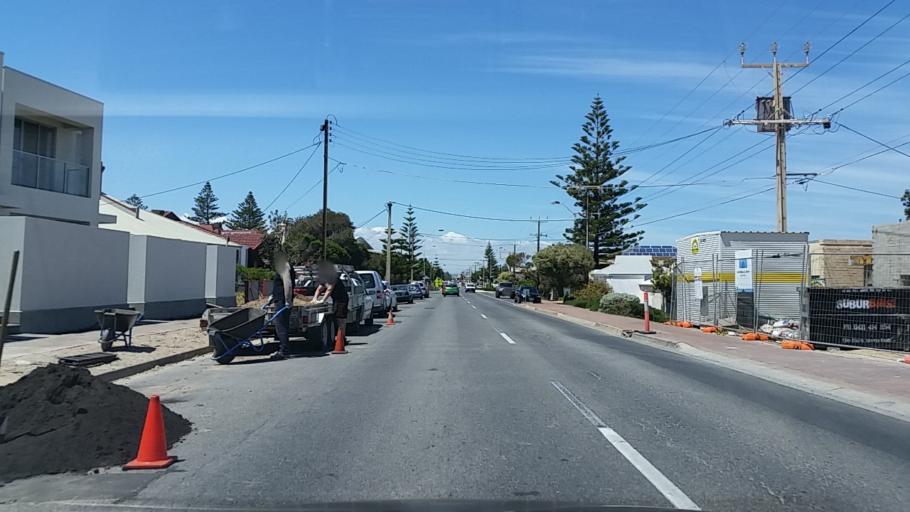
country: AU
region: South Australia
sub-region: Charles Sturt
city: Henley Beach
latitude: -34.9124
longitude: 138.4924
